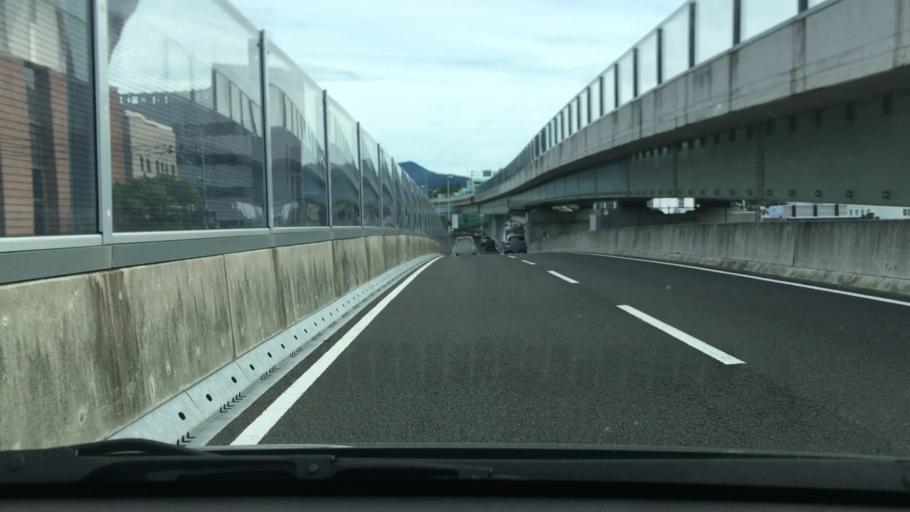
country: JP
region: Nagasaki
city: Nagasaki-shi
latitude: 32.7636
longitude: 129.8621
